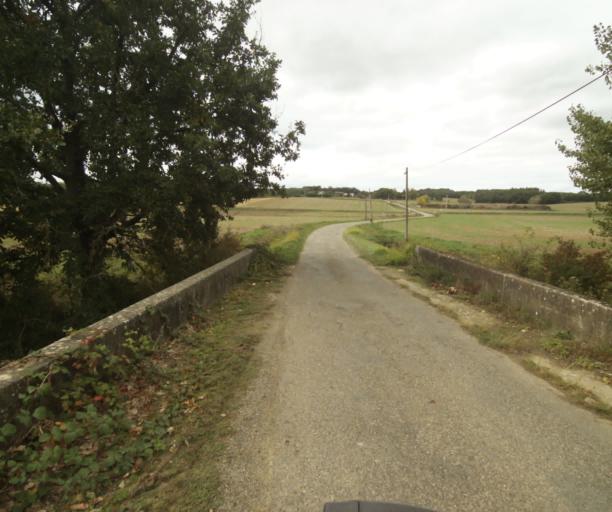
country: FR
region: Midi-Pyrenees
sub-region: Departement de la Haute-Garonne
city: Launac
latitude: 43.8391
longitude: 1.1107
